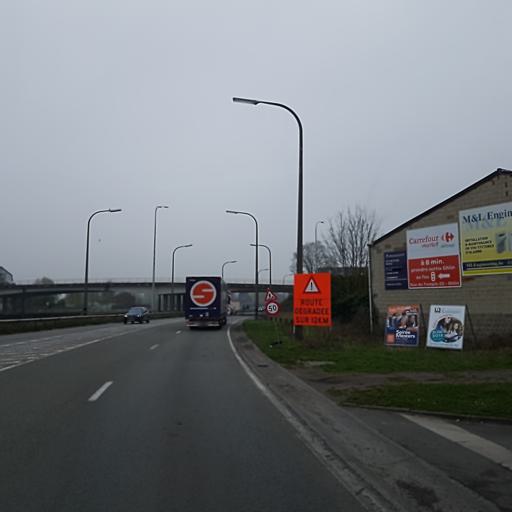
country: BE
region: Wallonia
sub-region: Province du Hainaut
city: Mons
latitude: 50.4800
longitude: 3.9505
